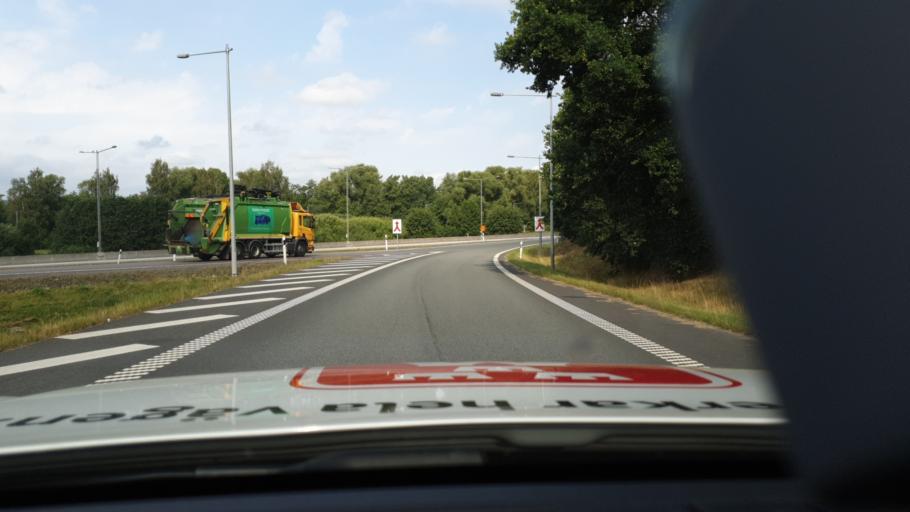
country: SE
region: Joenkoeping
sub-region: Jonkopings Kommun
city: Jonkoping
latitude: 57.7640
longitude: 14.1908
